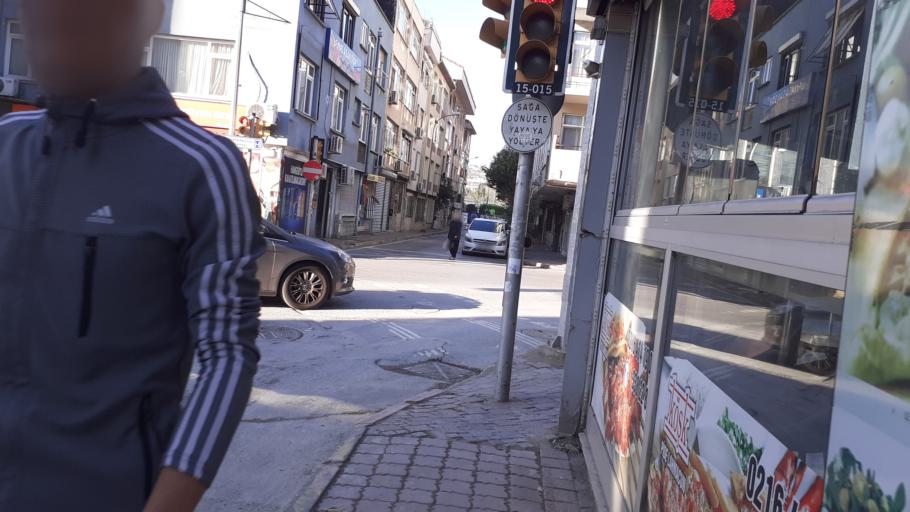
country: TR
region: Istanbul
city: UEskuedar
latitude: 40.9858
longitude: 29.0379
